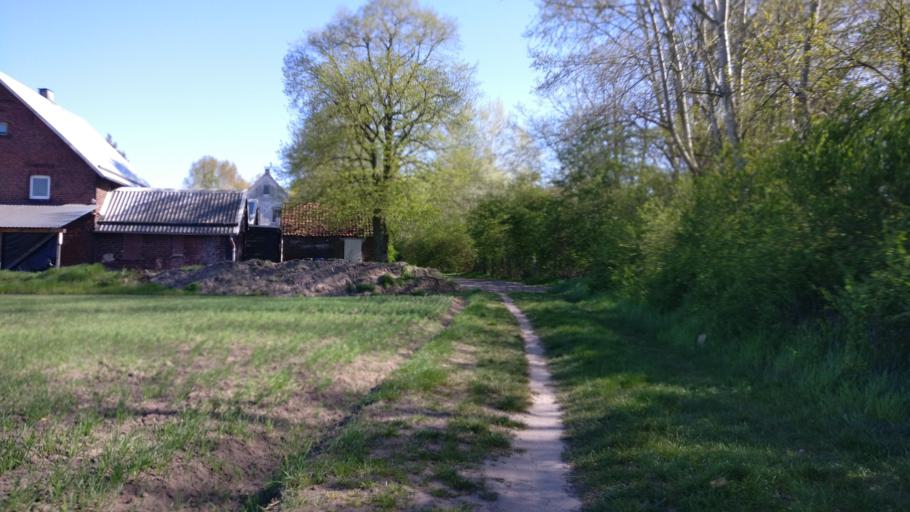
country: DE
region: North Rhine-Westphalia
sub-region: Regierungsbezirk Detmold
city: Lage
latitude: 52.0164
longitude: 8.7606
